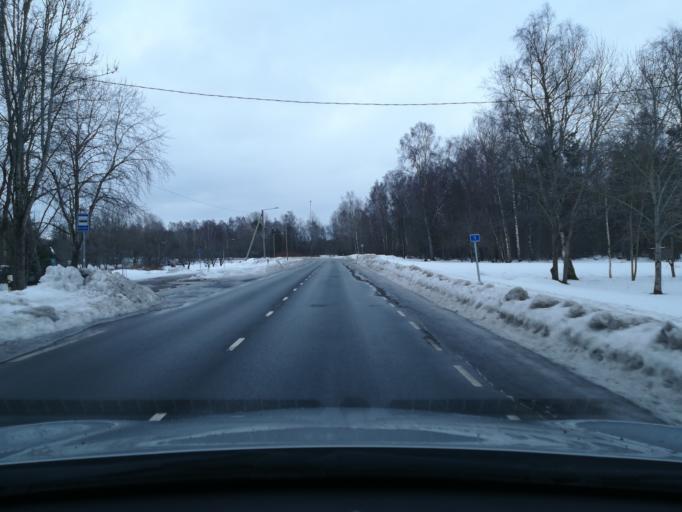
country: EE
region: Harju
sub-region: Nissi vald
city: Turba
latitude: 59.0753
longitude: 24.2401
